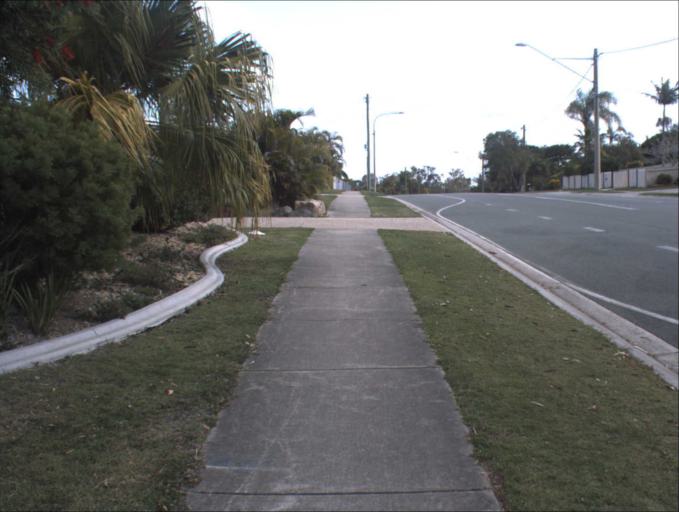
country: AU
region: Queensland
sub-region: Logan
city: Park Ridge South
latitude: -27.6766
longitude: 153.0379
